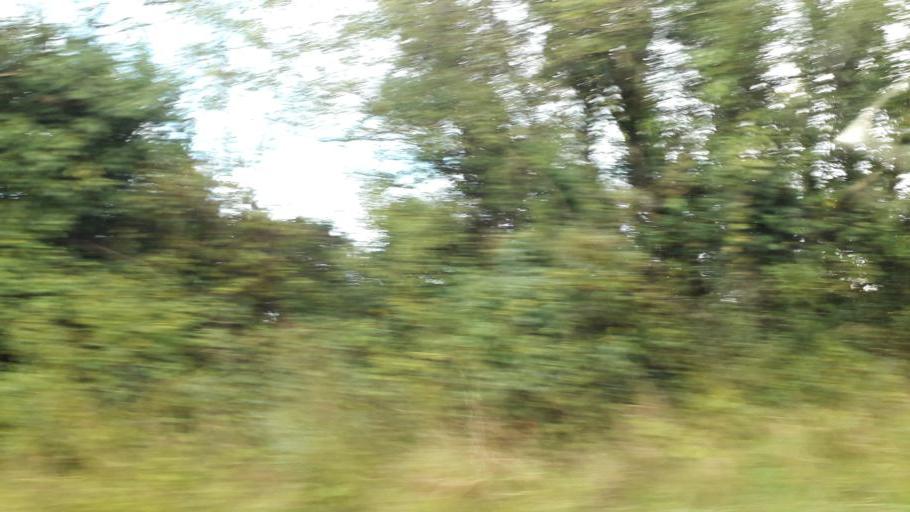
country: IE
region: Connaught
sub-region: Roscommon
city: Roscommon
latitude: 53.7742
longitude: -8.1292
